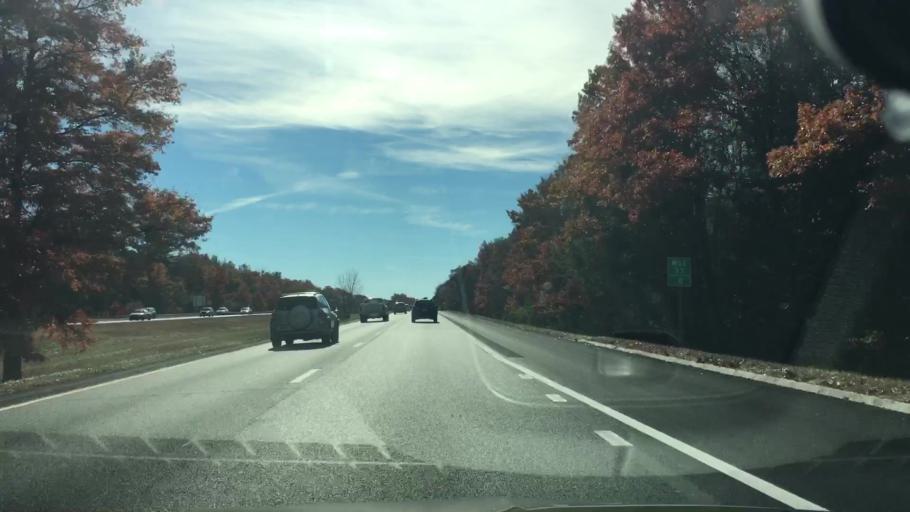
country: US
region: Massachusetts
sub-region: Franklin County
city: Whately
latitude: 42.4539
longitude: -72.6184
